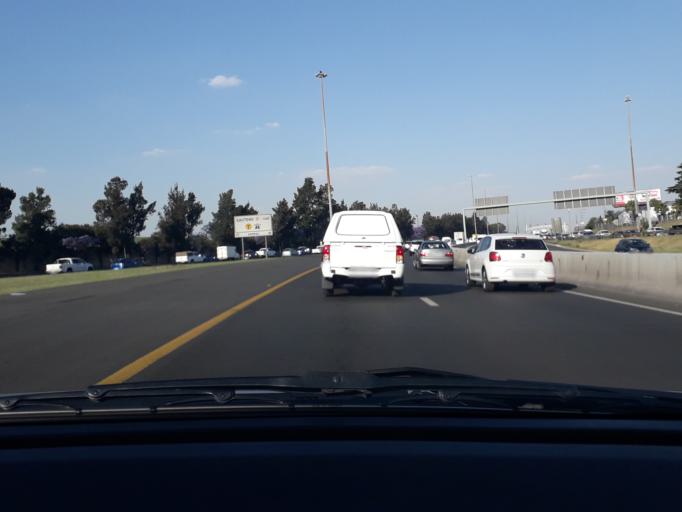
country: ZA
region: Gauteng
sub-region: Ekurhuleni Metropolitan Municipality
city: Germiston
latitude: -26.1684
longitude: 28.1358
